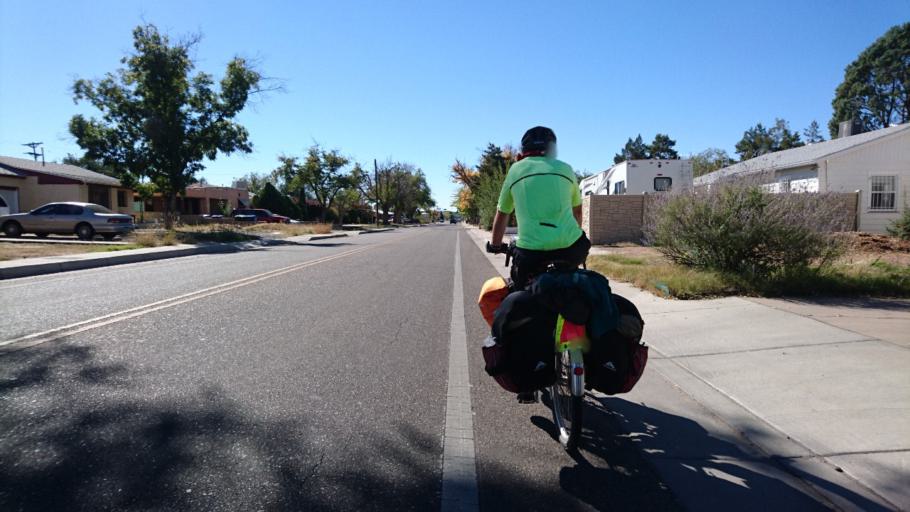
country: US
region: New Mexico
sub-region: Bernalillo County
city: Albuquerque
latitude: 35.0826
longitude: -106.5954
